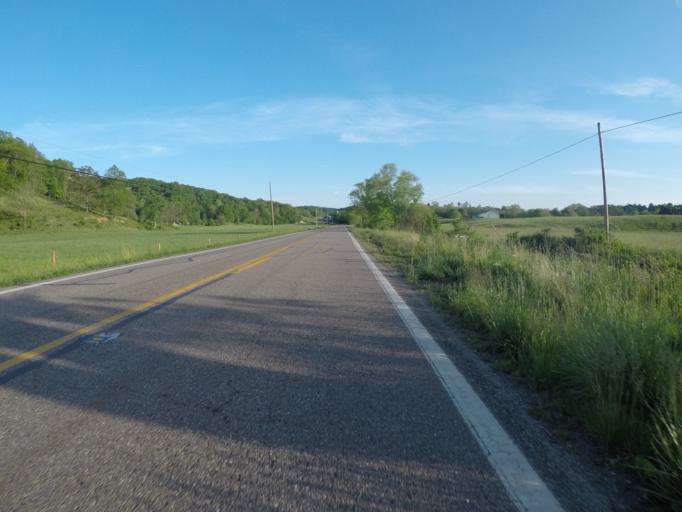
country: US
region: West Virginia
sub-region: Cabell County
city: Huntington
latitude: 38.5403
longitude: -82.4609
